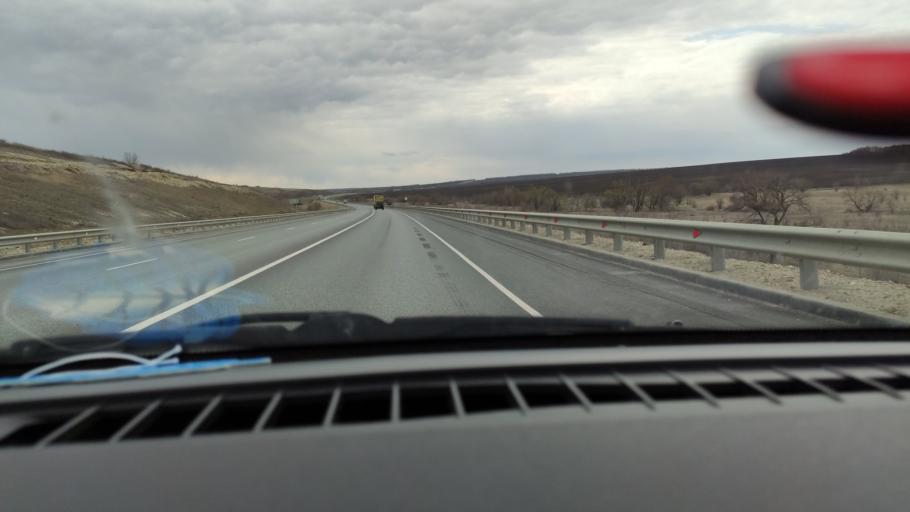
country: RU
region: Saratov
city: Yelshanka
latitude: 51.8697
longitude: 46.5033
